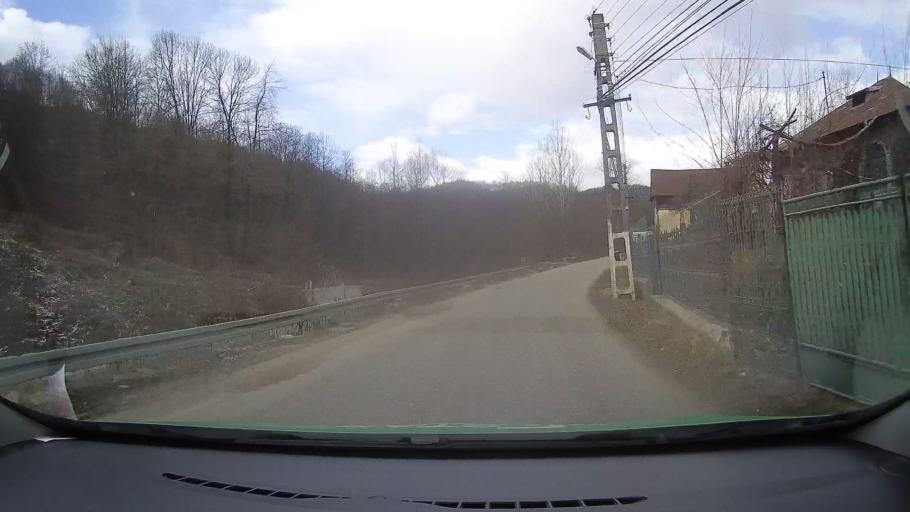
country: RO
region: Dambovita
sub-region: Comuna Visinesti
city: Visinesti
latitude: 45.1040
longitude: 25.5583
